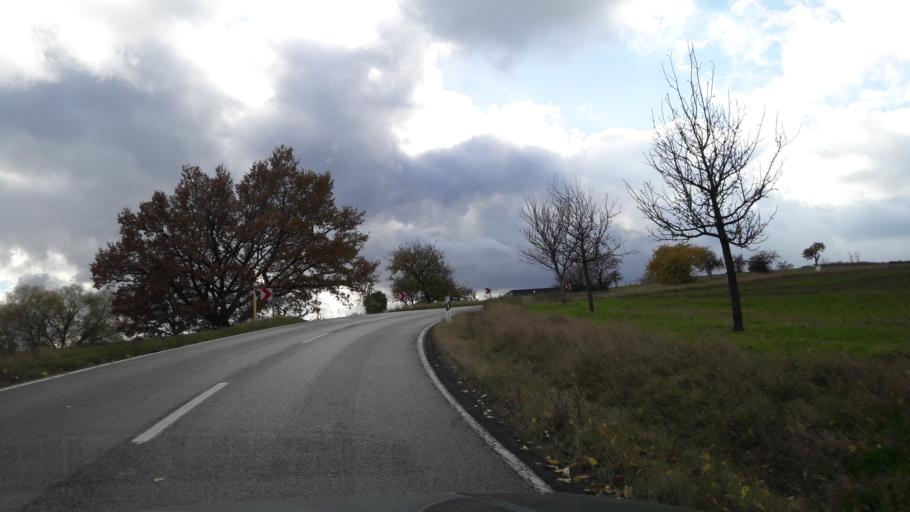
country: DE
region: Rheinland-Pfalz
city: Krottelbach
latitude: 49.4614
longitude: 7.3347
